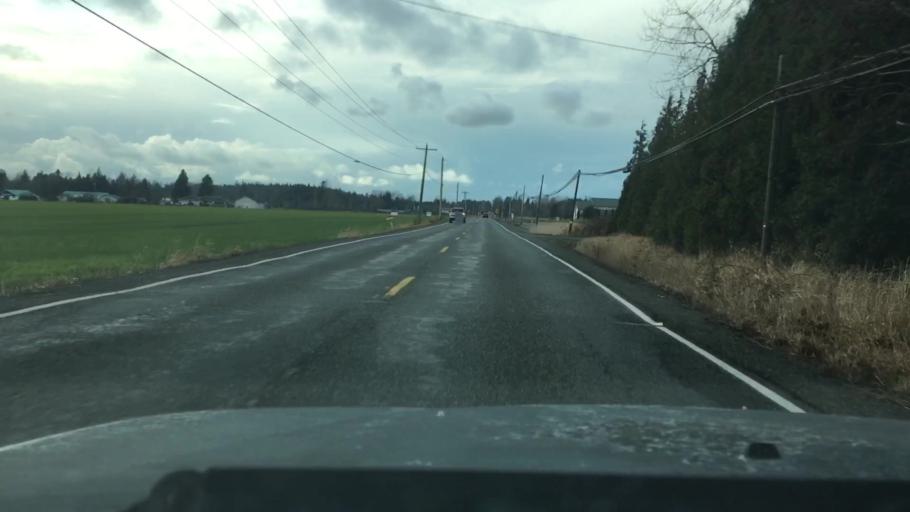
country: US
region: Washington
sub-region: Whatcom County
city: Ferndale
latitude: 48.8484
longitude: -122.6333
